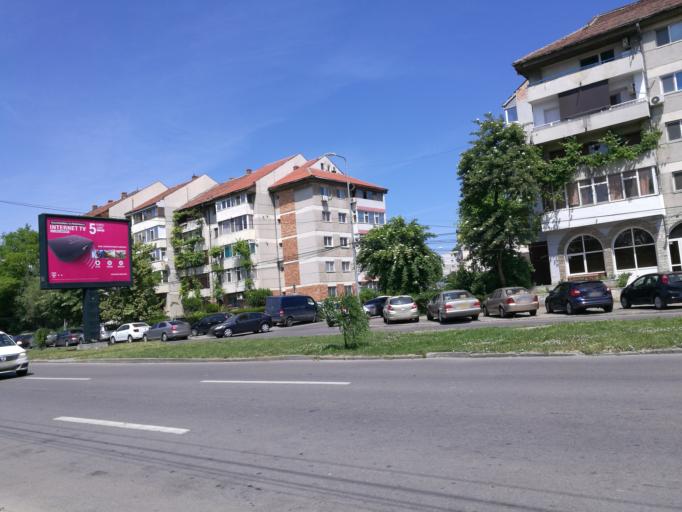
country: RO
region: Constanta
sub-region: Municipiul Constanta
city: Constanta
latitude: 44.2063
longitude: 28.6437
